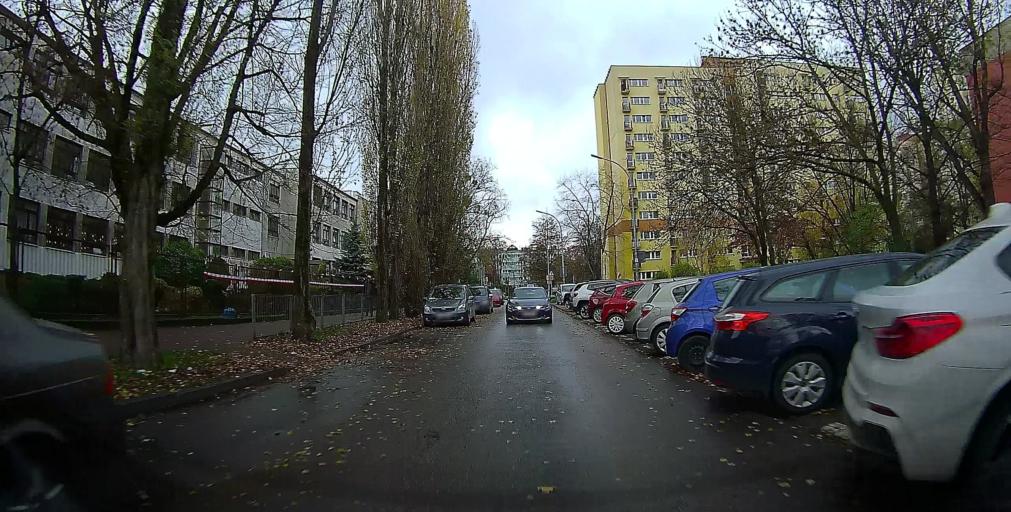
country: PL
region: Masovian Voivodeship
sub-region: Warszawa
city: Ochota
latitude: 52.1955
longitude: 20.9787
